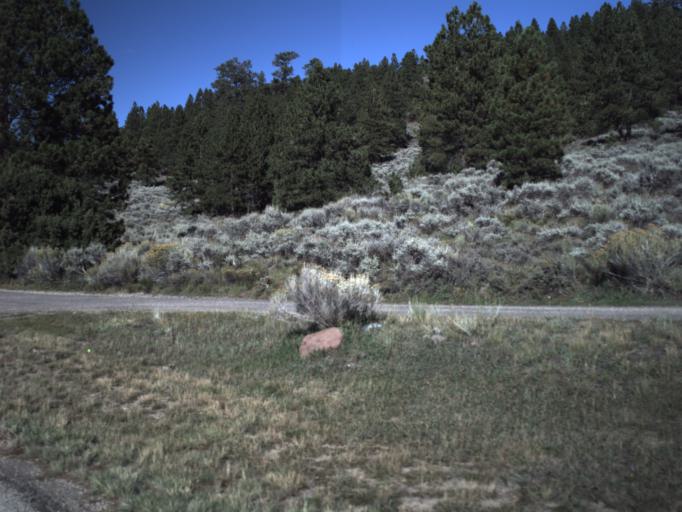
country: US
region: Utah
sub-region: Garfield County
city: Panguitch
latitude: 37.7143
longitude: -112.6231
